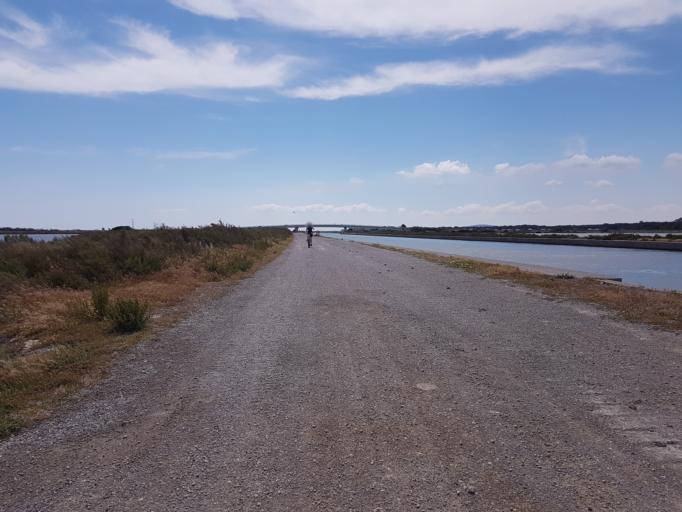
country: FR
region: Languedoc-Roussillon
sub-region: Departement de l'Herault
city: Vic-la-Gardiole
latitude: 43.4682
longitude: 3.8219
